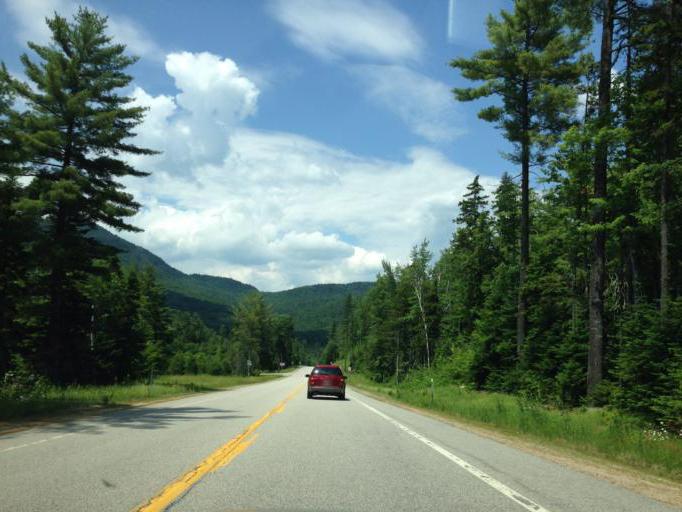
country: US
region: New Hampshire
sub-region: Carroll County
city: Tamworth
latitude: 43.9999
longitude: -71.2769
